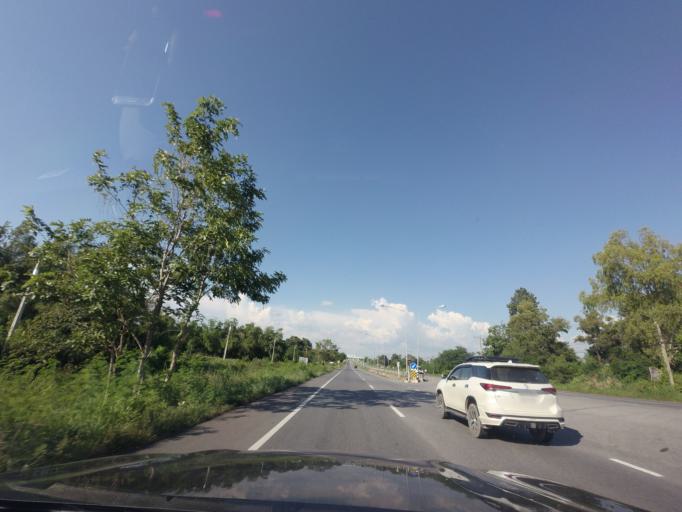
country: TH
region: Khon Kaen
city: Non Sila
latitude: 15.9472
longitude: 102.6808
